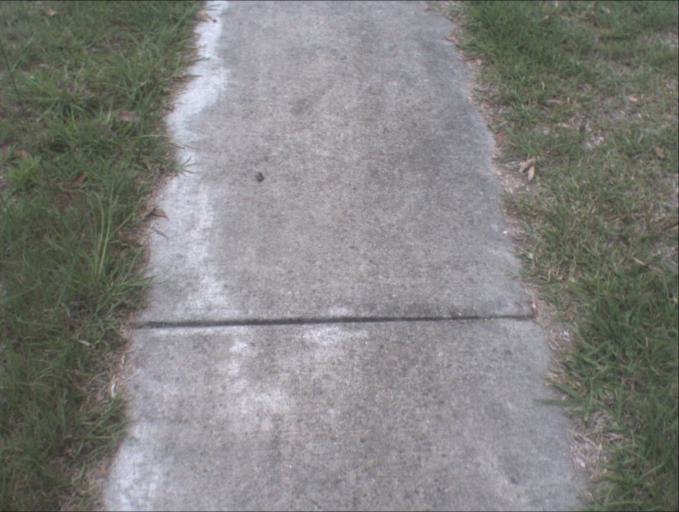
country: AU
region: Queensland
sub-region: Ipswich
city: Springfield Lakes
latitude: -27.7281
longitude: 152.9359
